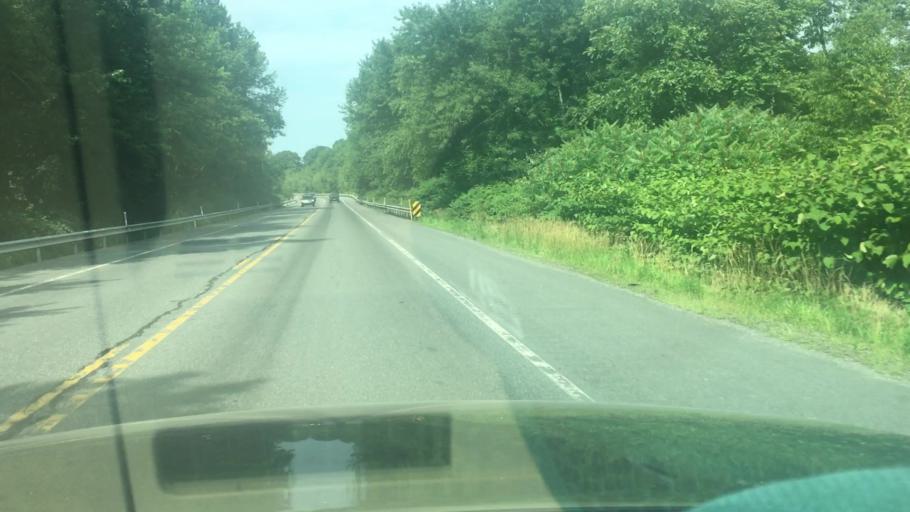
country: US
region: Pennsylvania
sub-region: Northumberland County
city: Mount Carmel
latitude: 40.7916
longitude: -76.4391
